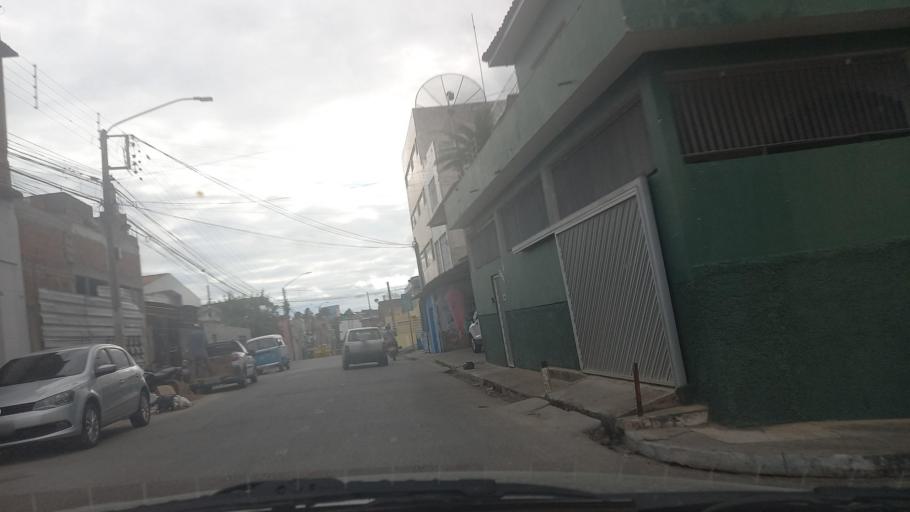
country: BR
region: Pernambuco
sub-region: Caruaru
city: Caruaru
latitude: -8.2943
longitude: -35.9772
